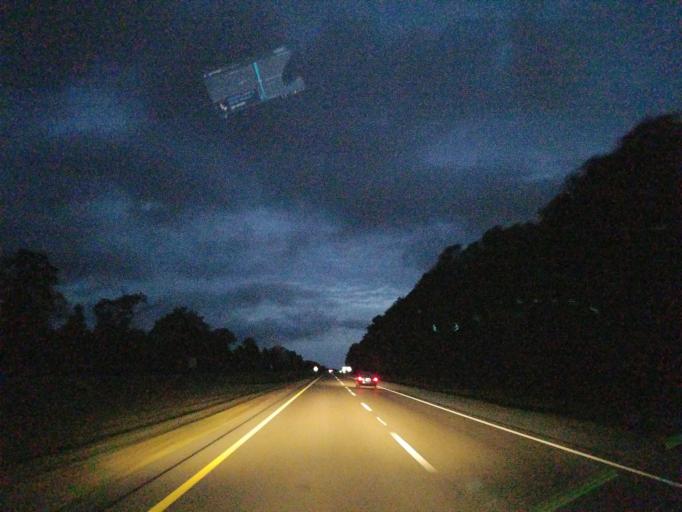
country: US
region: Mississippi
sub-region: Jones County
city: Sharon
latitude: 31.7959
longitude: -89.0546
